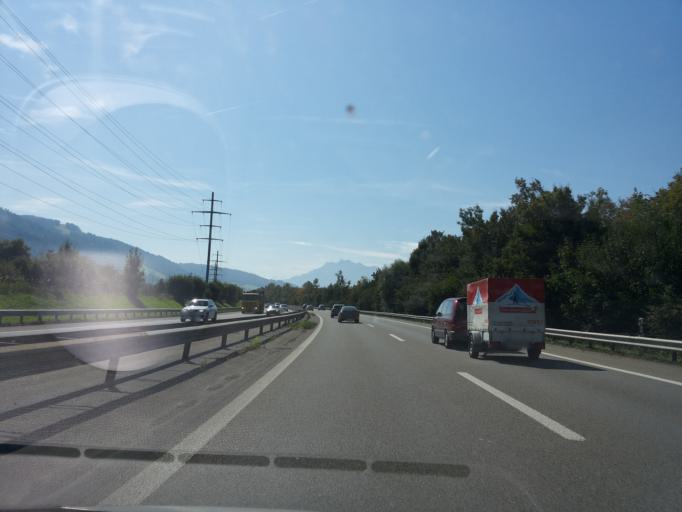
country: CH
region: Lucerne
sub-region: Lucerne-Land District
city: Root
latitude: 47.1347
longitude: 8.3995
